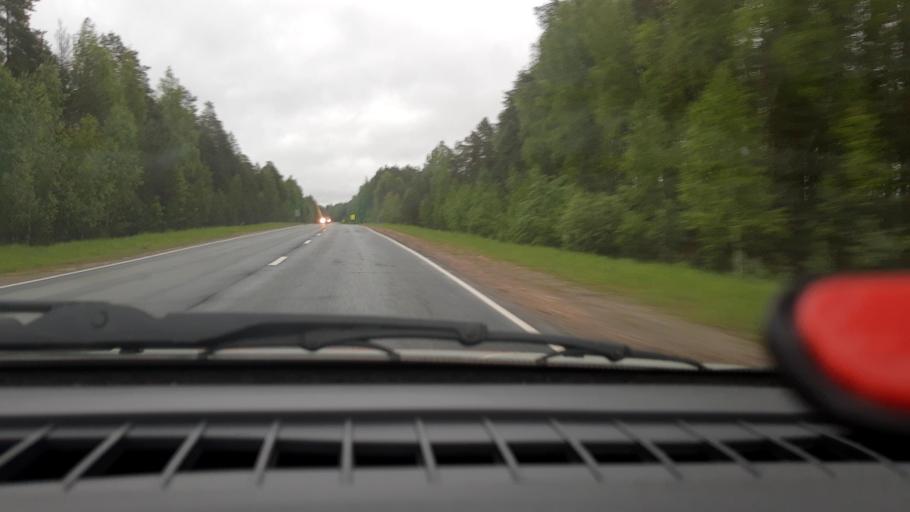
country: RU
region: Nizjnij Novgorod
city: Krasnyye Baki
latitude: 57.1779
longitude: 45.3392
